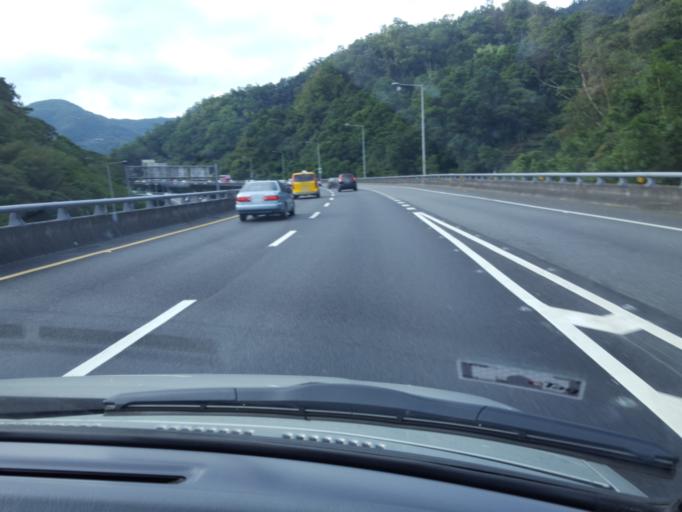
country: TW
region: Taiwan
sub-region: Keelung
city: Keelung
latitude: 24.9439
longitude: 121.7113
